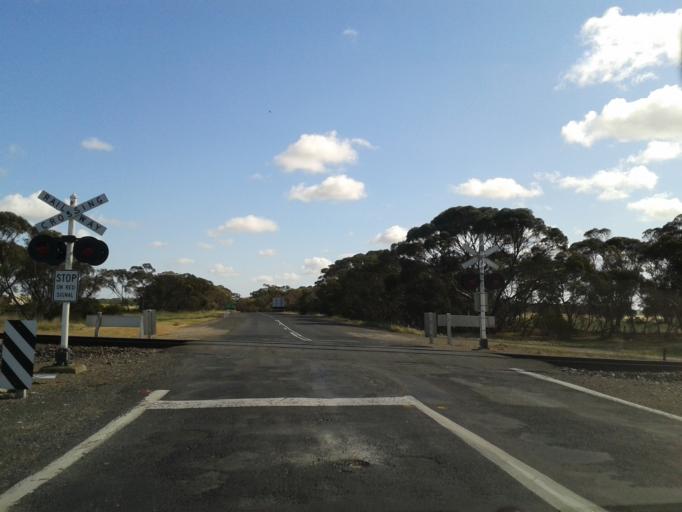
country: AU
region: South Australia
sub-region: Tatiara
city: Bordertown
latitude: -36.2528
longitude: 140.6737
